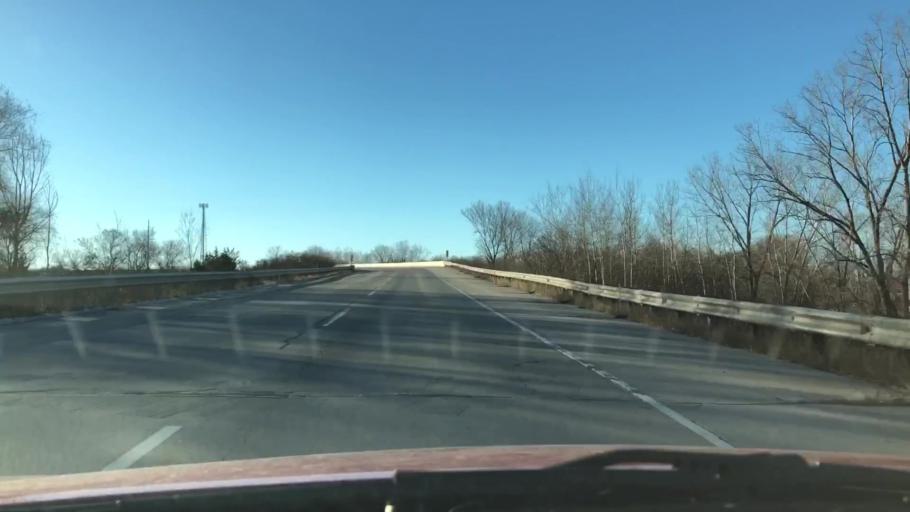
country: US
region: Wisconsin
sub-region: Brown County
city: De Pere
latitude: 44.4563
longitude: -88.0854
